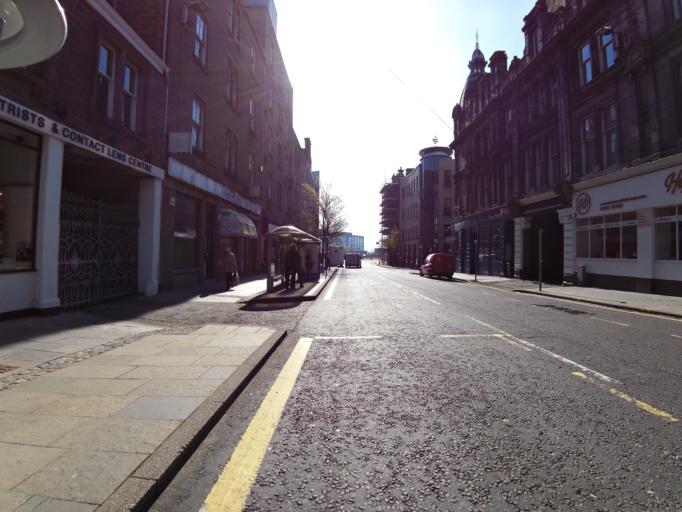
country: GB
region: Scotland
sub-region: Dundee City
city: Dundee
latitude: 56.4610
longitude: -2.9672
